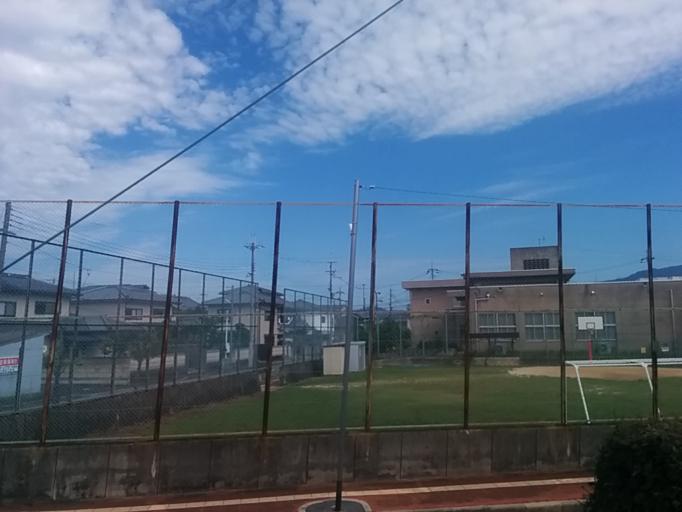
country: JP
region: Nara
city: Kashihara-shi
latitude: 34.4986
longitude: 135.7937
